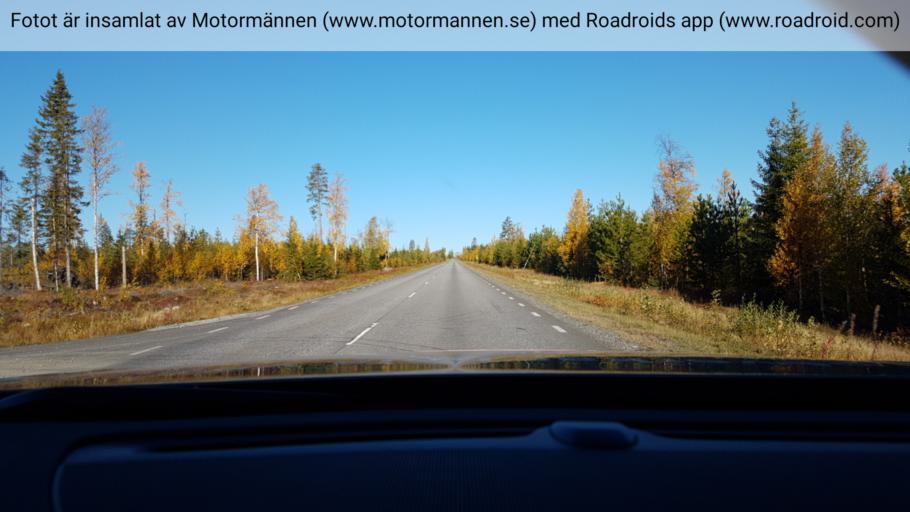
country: SE
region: Vaesterbotten
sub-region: Skelleftea Kommun
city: Storvik
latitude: 65.3431
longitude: 20.5154
